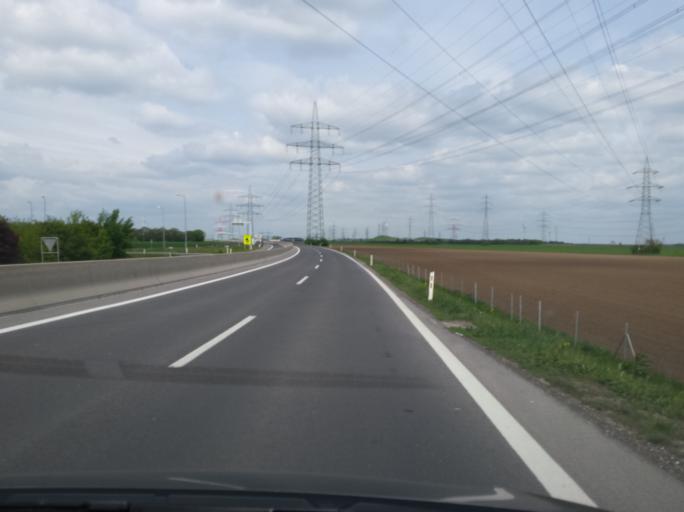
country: AT
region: Lower Austria
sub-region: Politischer Bezirk Wien-Umgebung
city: Leopoldsdorf
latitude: 48.1069
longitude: 16.4147
